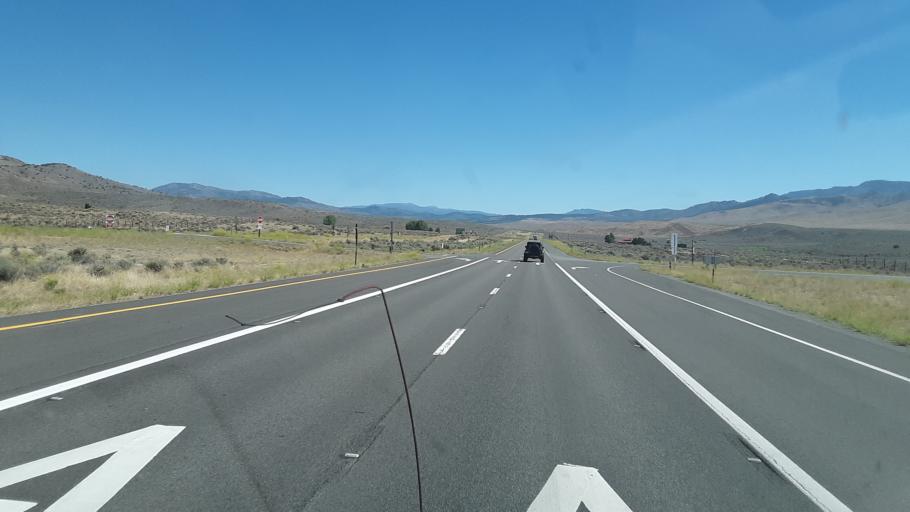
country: US
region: Nevada
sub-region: Washoe County
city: Cold Springs
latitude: 39.7389
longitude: -120.0396
